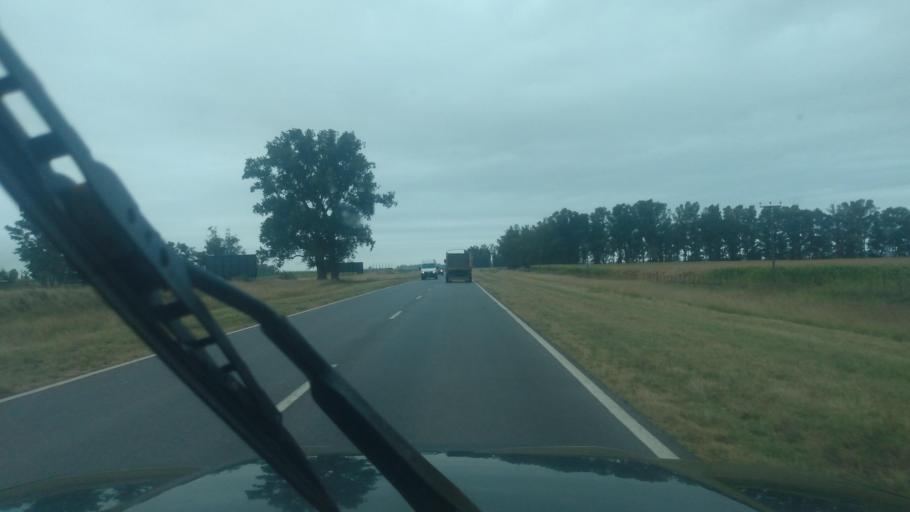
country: AR
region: Buenos Aires
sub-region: Partido de Nueve de Julio
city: Nueve de Julio
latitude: -35.4053
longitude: -60.7703
